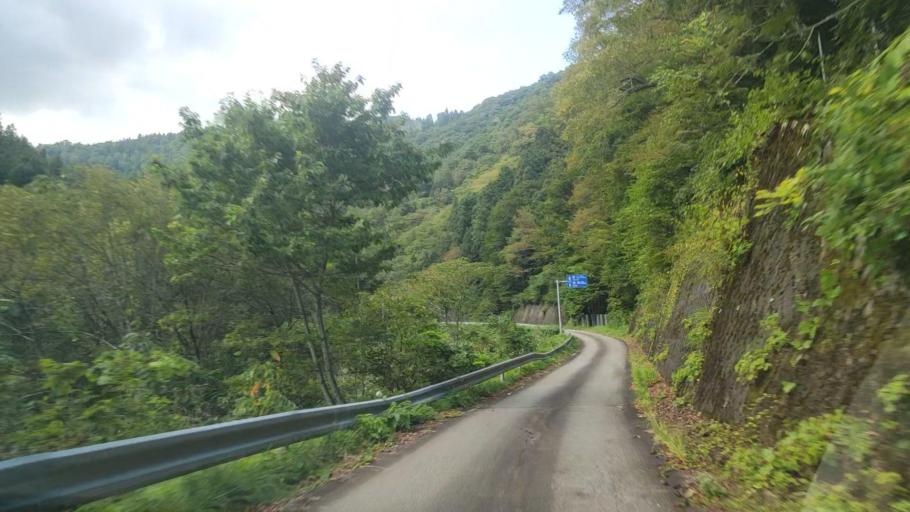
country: JP
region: Gifu
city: Takayama
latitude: 36.3106
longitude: 137.0937
